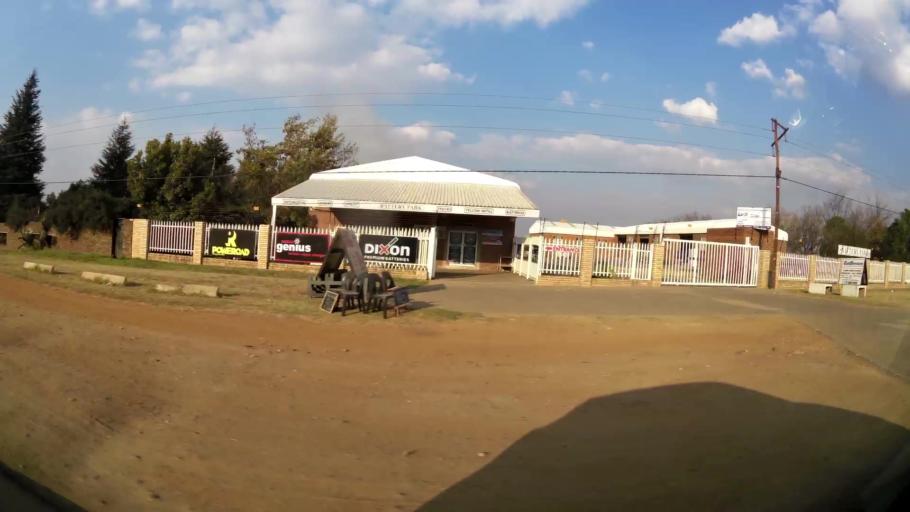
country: ZA
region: Gauteng
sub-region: Ekurhuleni Metropolitan Municipality
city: Benoni
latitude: -26.1172
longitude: 28.2946
